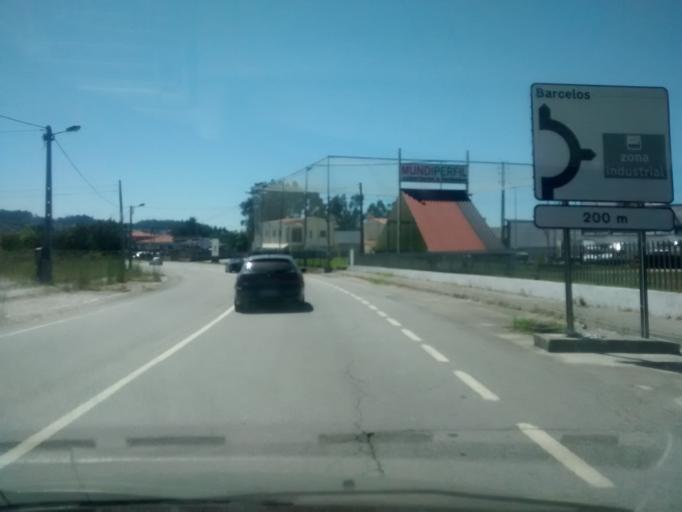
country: PT
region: Braga
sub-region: Barcelos
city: Galegos
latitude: 41.5212
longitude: -8.5745
